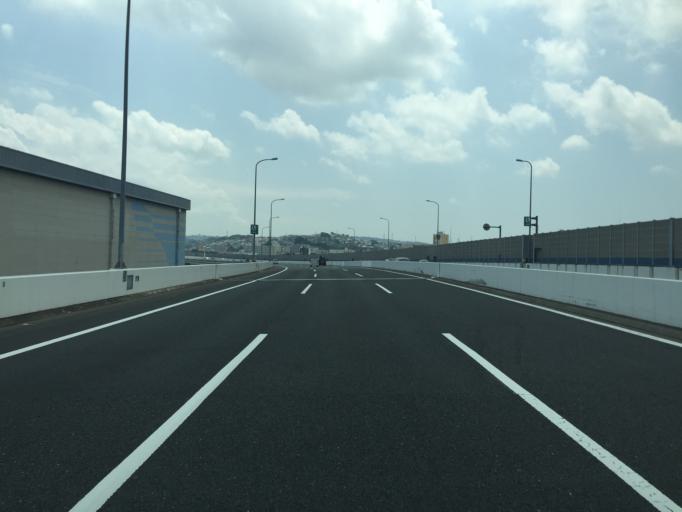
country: JP
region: Kanagawa
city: Yokohama
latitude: 35.3974
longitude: 139.6174
